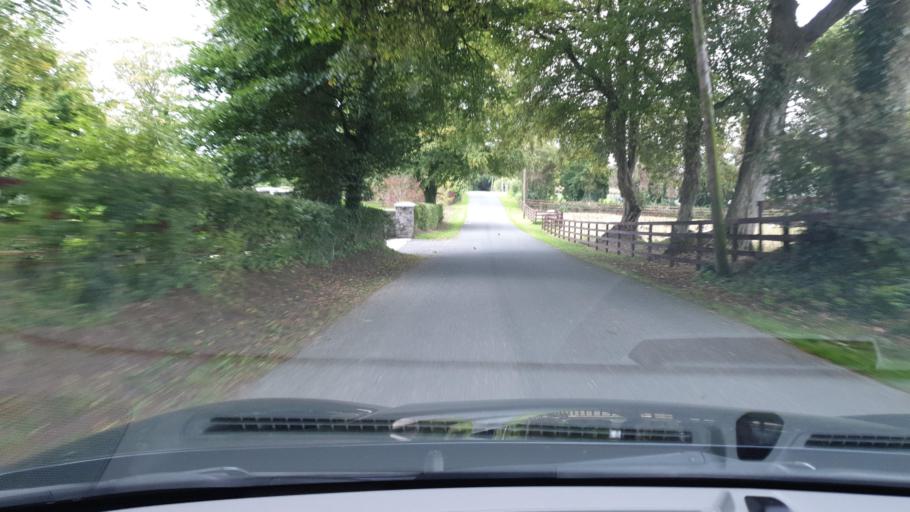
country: IE
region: Leinster
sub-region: An Mhi
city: Dunshaughlin
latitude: 53.4883
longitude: -6.5835
